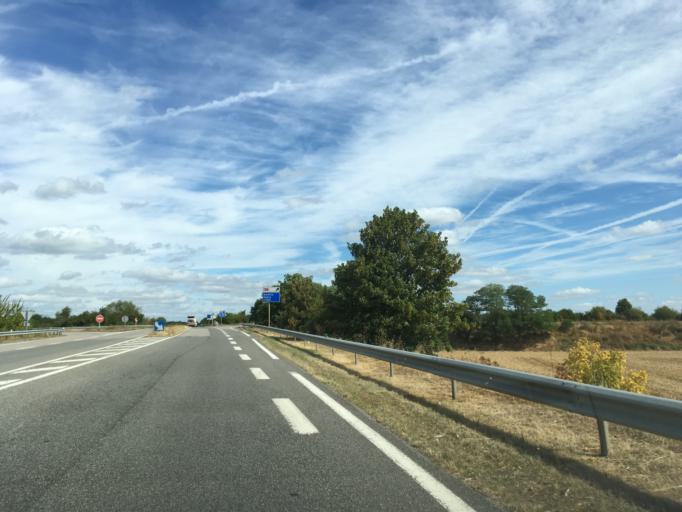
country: FR
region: Haute-Normandie
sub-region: Departement de l'Eure
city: Saint-Aubin-sur-Gaillon
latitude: 49.1332
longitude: 1.3118
